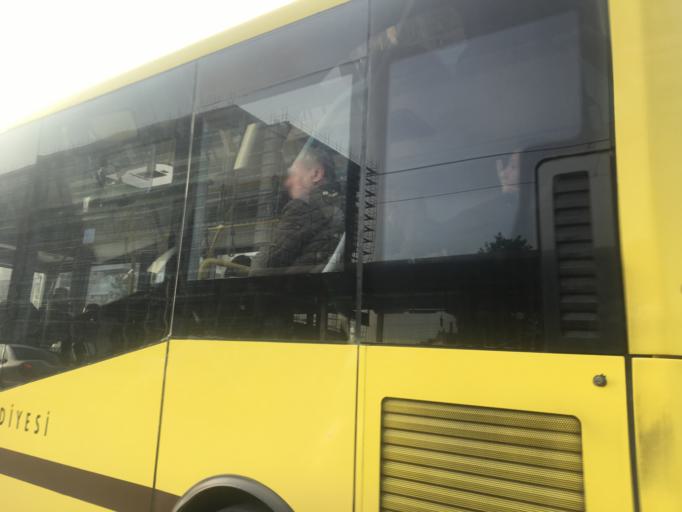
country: TR
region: Bursa
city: Yildirim
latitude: 40.2120
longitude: 28.9878
